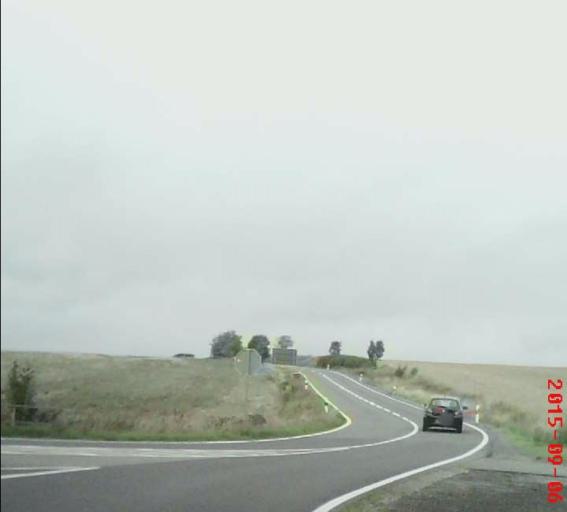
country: DE
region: Thuringia
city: Muehlhausen
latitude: 51.2466
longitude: 10.4526
